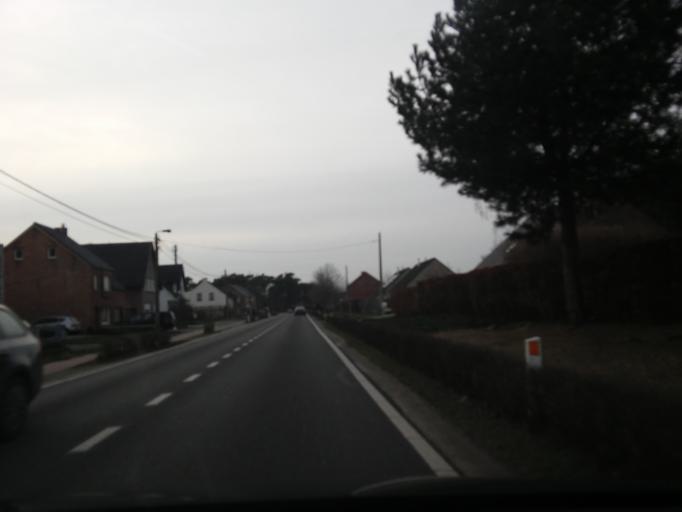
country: BE
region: Flanders
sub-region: Provincie Antwerpen
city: Herselt
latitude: 51.0464
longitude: 4.9182
